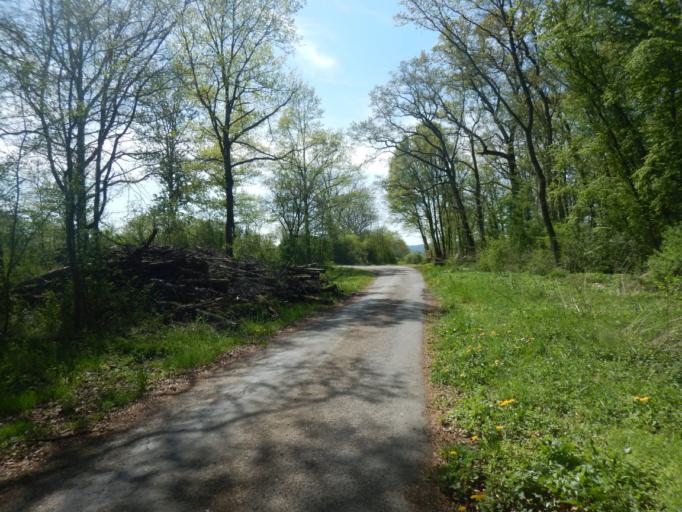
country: LU
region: Diekirch
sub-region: Canton de Redange
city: Redange-sur-Attert
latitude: 49.7495
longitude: 5.9298
